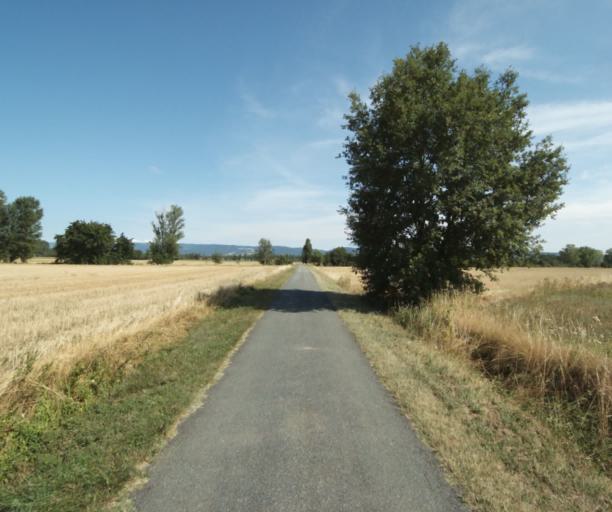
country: FR
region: Midi-Pyrenees
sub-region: Departement de la Haute-Garonne
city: Revel
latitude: 43.4987
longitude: 1.9813
